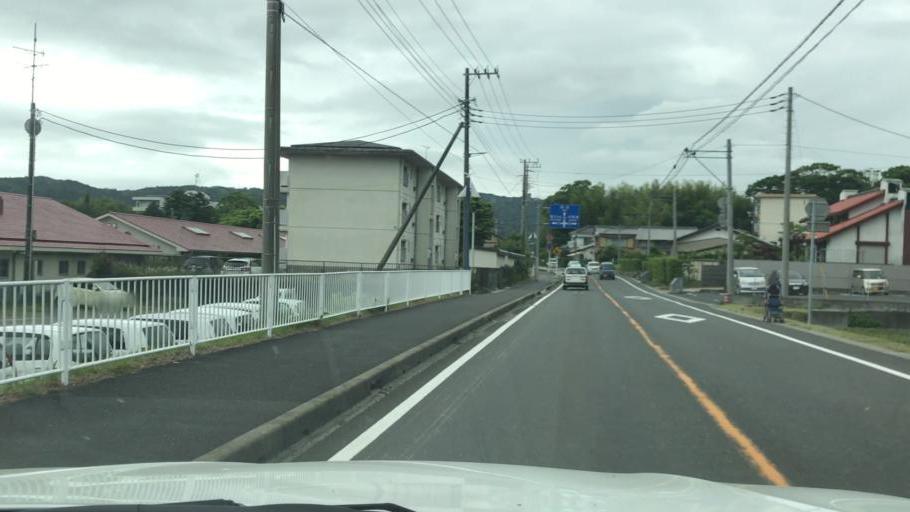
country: JP
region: Chiba
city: Kawaguchi
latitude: 35.1233
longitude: 140.0858
